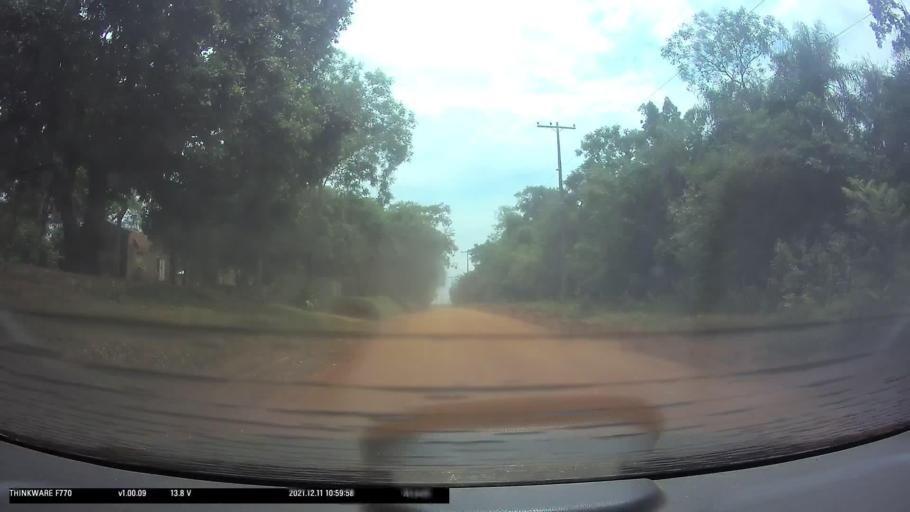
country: PY
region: Cordillera
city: San Bernardino
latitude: -25.3075
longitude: -57.2528
